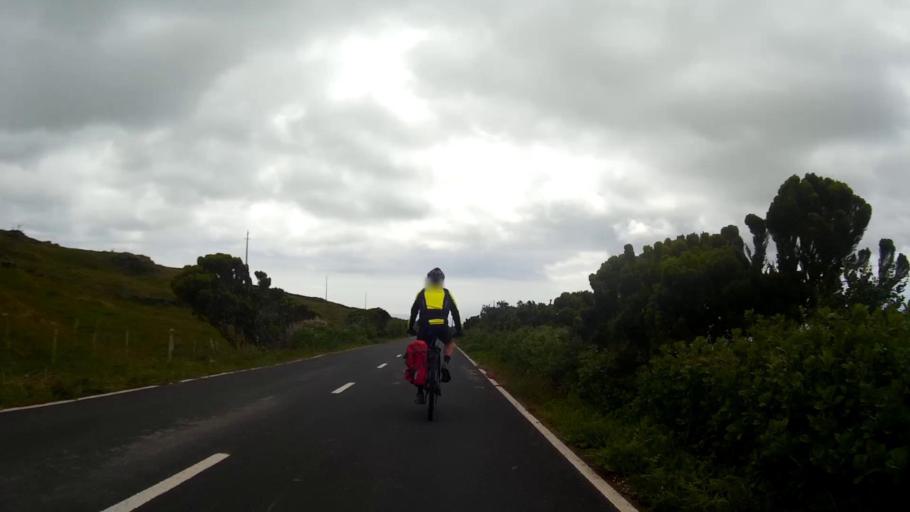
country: PT
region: Azores
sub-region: Madalena
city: Madalena
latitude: 38.4972
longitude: -28.4290
